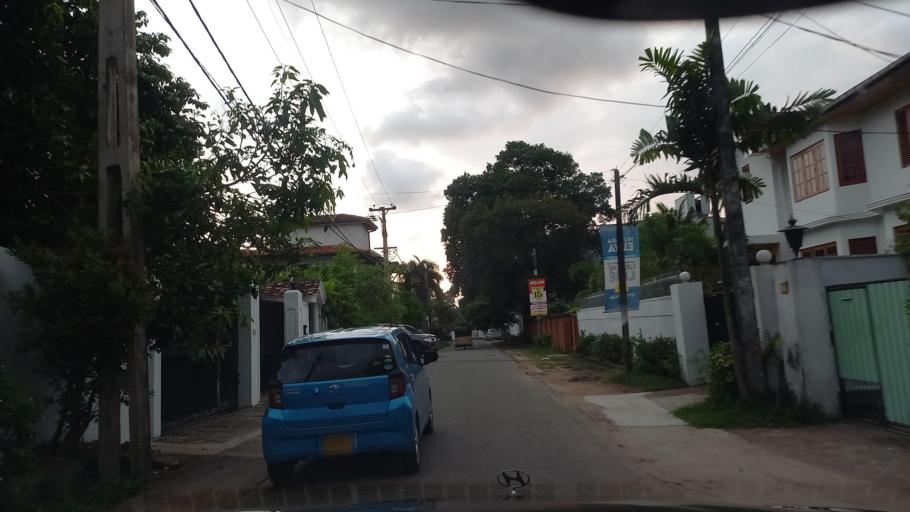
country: LK
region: Western
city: Battaramulla South
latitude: 6.8969
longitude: 79.9171
